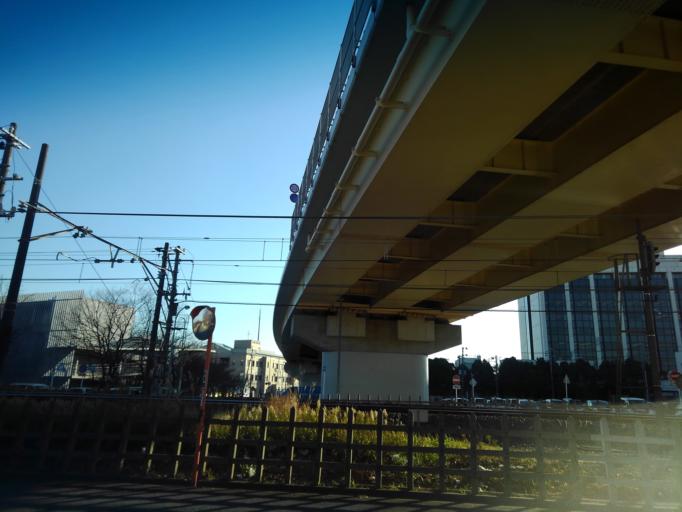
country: JP
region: Chiba
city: Kimitsu
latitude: 35.3317
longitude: 139.9035
